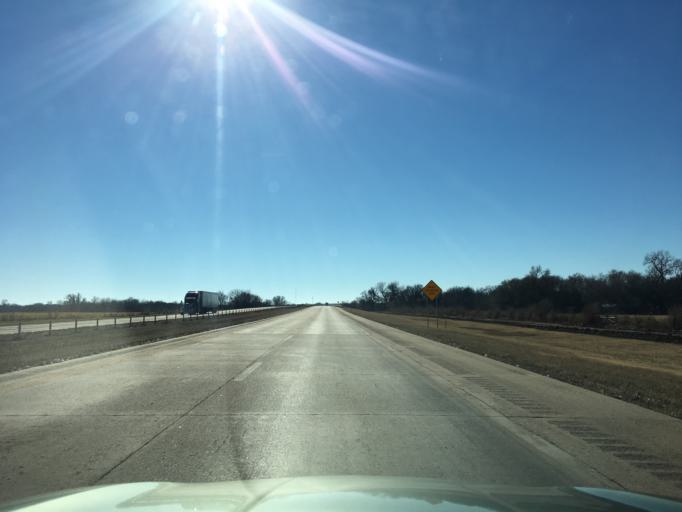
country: US
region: Oklahoma
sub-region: Kay County
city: Blackwell
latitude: 36.9120
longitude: -97.3523
